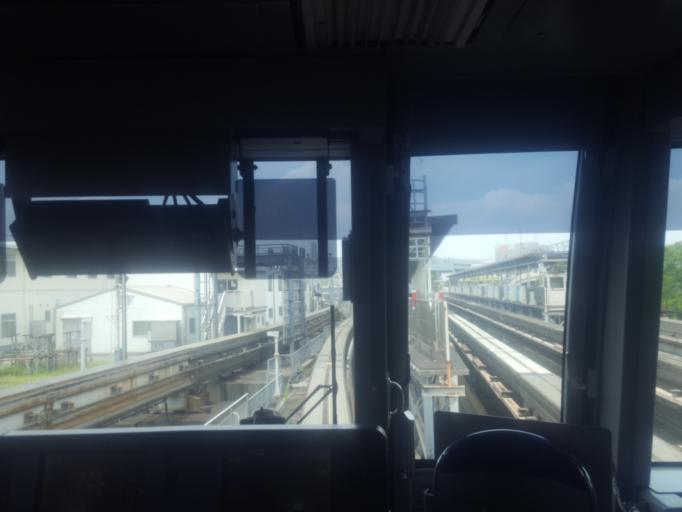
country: JP
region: Kanagawa
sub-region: Kawasaki-shi
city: Kawasaki
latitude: 35.5698
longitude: 139.7497
